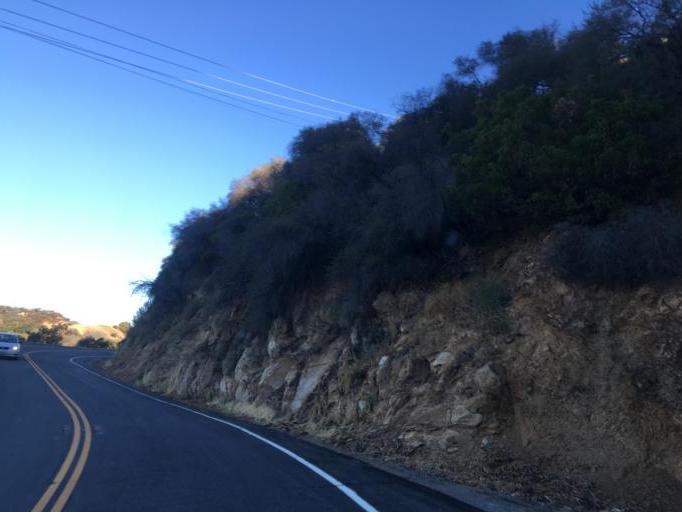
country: US
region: California
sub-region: Los Angeles County
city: Westlake Village
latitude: 34.0865
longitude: -118.8067
